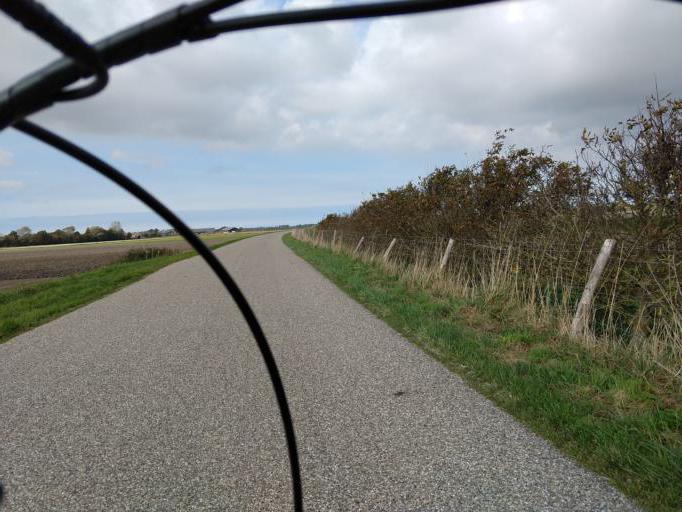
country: NL
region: Zeeland
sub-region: Schouwen-Duiveland
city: Scharendijke
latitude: 51.6899
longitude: 3.9510
